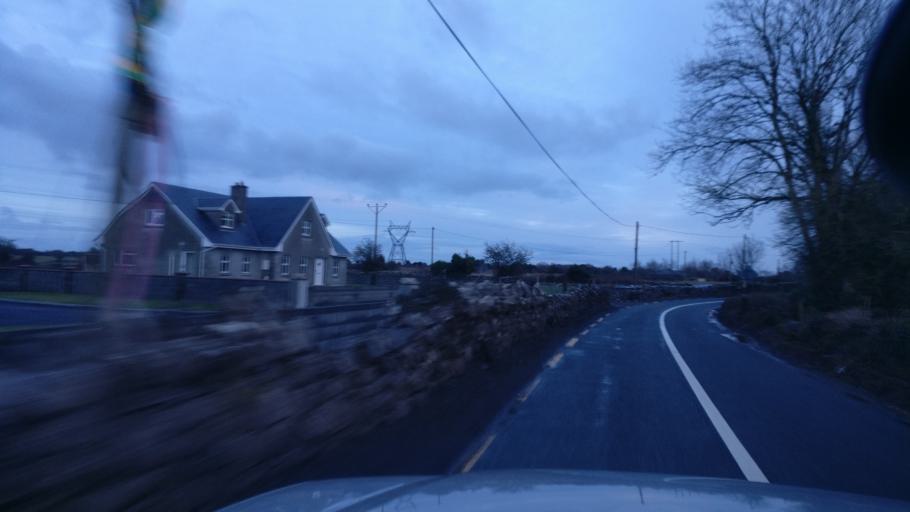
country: IE
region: Connaught
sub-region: County Galway
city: Athenry
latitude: 53.2517
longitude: -8.6693
